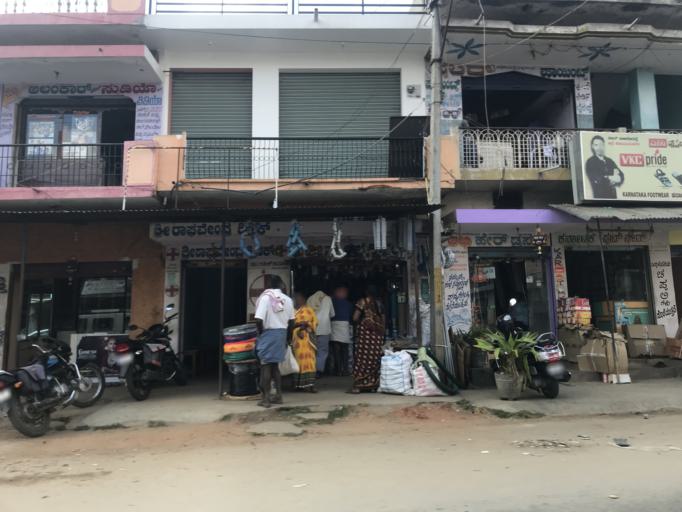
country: IN
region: Karnataka
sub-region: Mandya
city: Krishnarajpet
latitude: 12.7622
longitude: 76.4256
